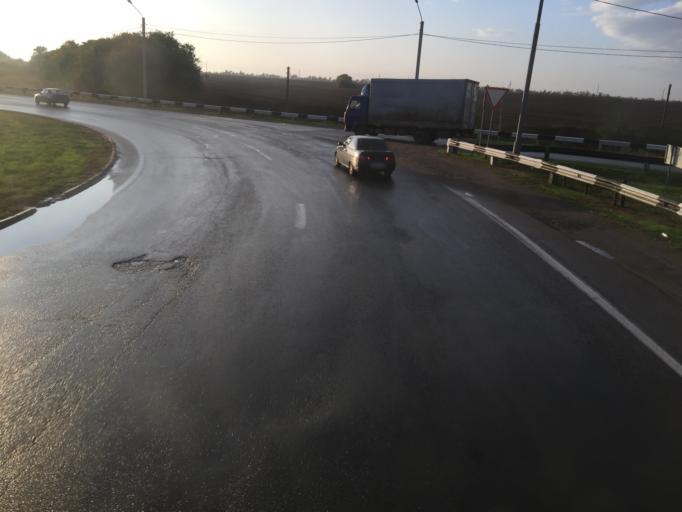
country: RU
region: Rostov
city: Bataysk
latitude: 47.0814
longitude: 39.7730
